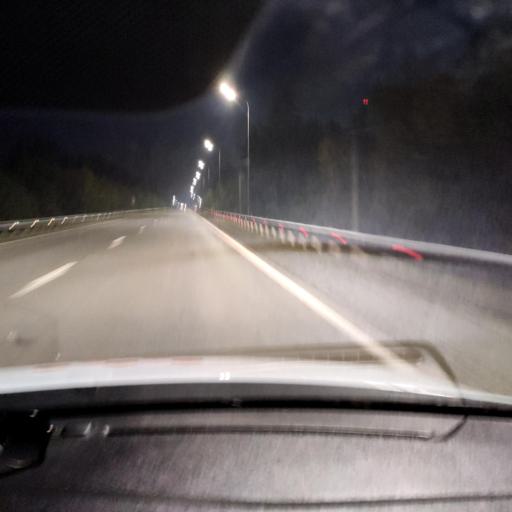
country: RU
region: Tatarstan
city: Stolbishchi
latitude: 55.6362
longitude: 49.1075
